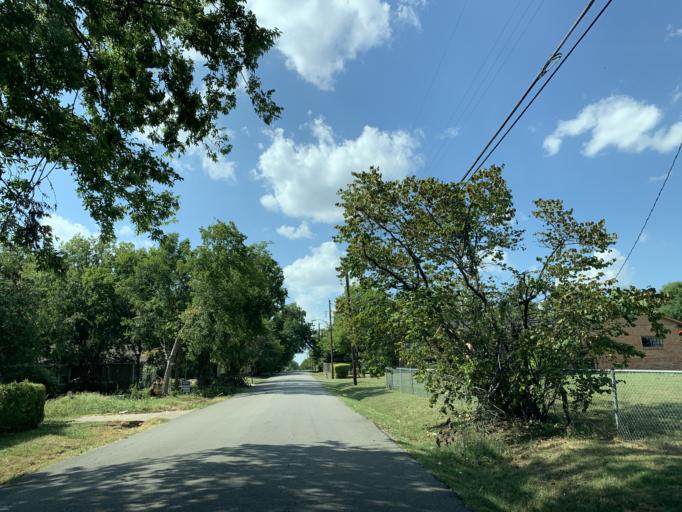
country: US
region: Texas
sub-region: Dallas County
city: Hutchins
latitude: 32.6927
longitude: -96.7772
